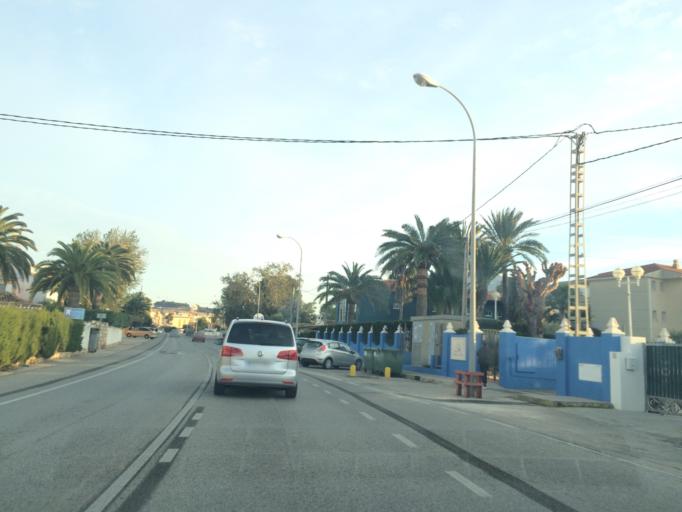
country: ES
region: Valencia
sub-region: Provincia de Alicante
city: Denia
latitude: 38.8511
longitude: 0.0934
